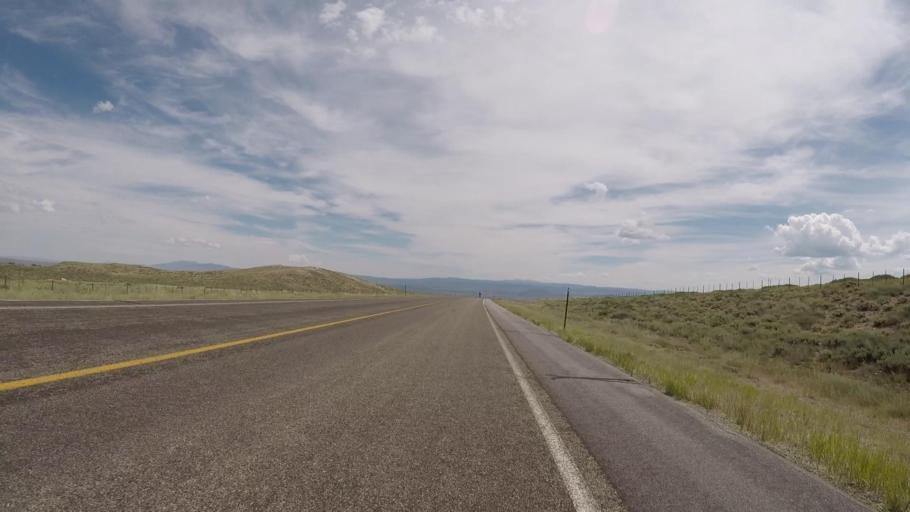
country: US
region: Wyoming
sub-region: Carbon County
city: Saratoga
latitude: 41.2009
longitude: -106.8326
